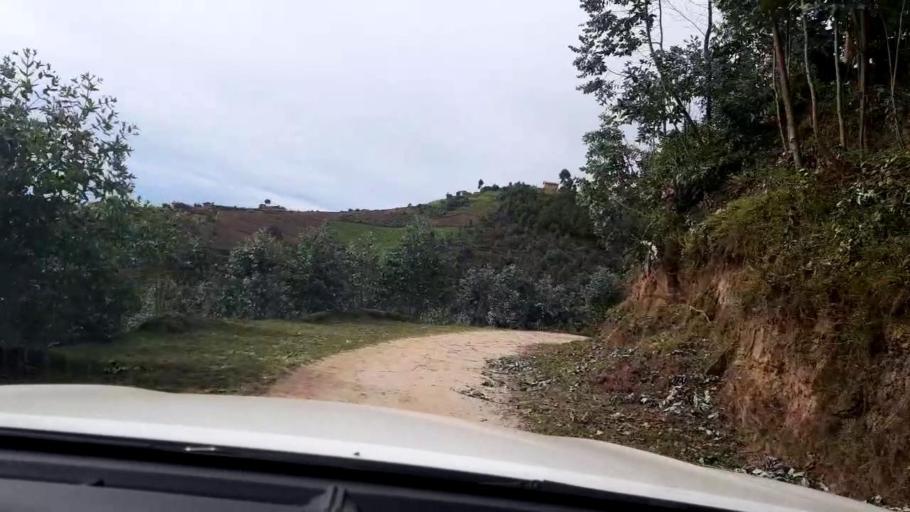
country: RW
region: Western Province
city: Kibuye
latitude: -1.8888
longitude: 29.4515
